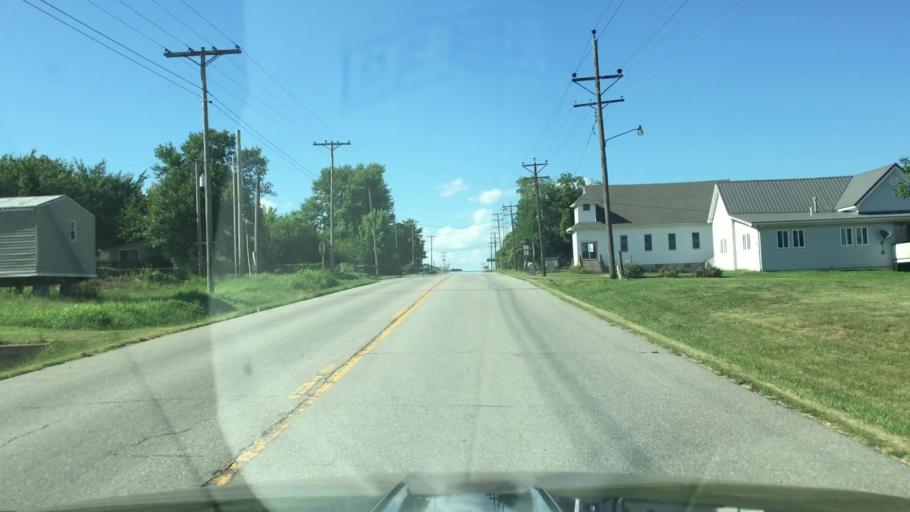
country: US
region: Missouri
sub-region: Moniteau County
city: Tipton
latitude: 38.5661
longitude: -92.7970
